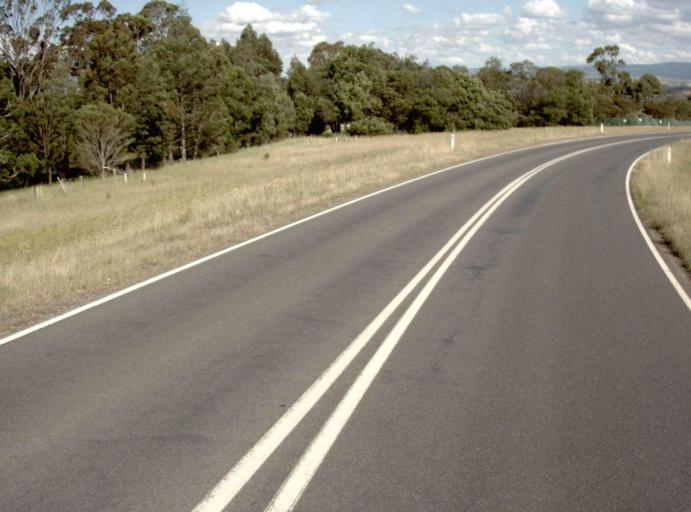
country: AU
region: Victoria
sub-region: Latrobe
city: Moe
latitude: -38.1973
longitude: 146.3268
